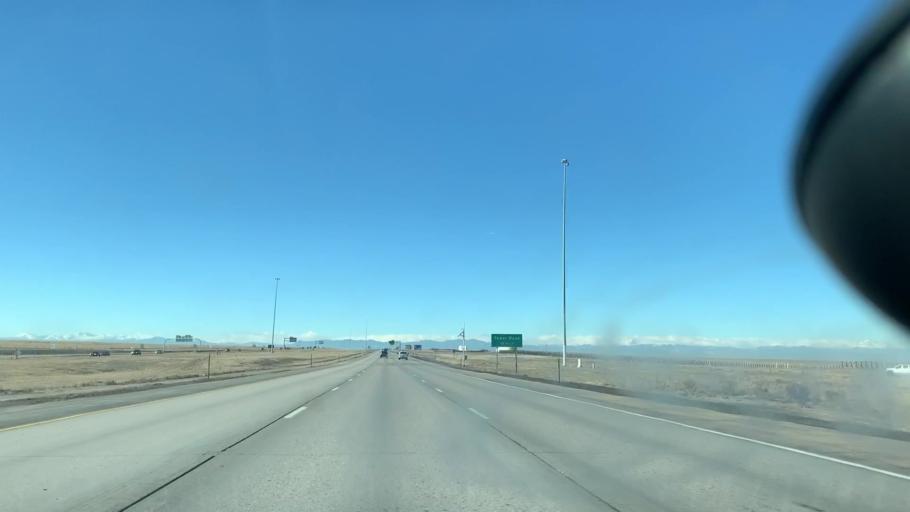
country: US
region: Colorado
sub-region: Adams County
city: Aurora
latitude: 39.8346
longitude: -104.7507
